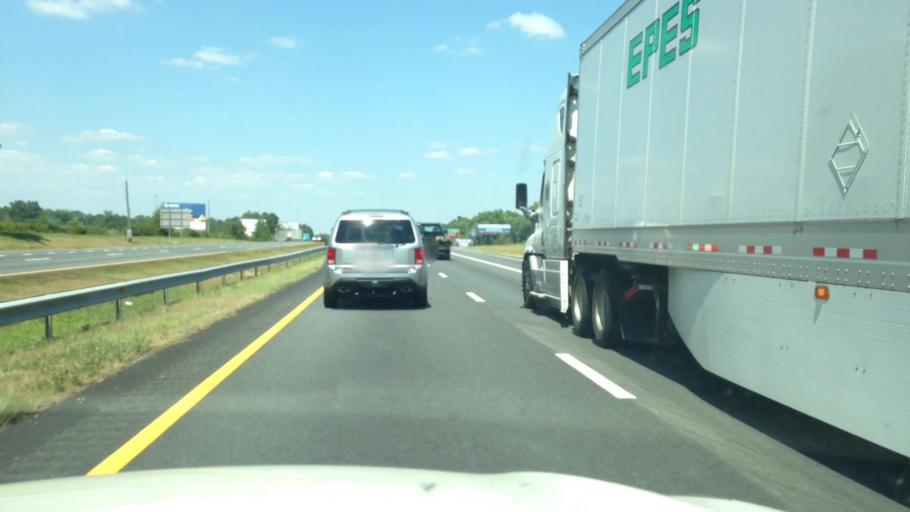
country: US
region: North Carolina
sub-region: Johnston County
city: Benson
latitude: 35.3789
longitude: -78.5366
